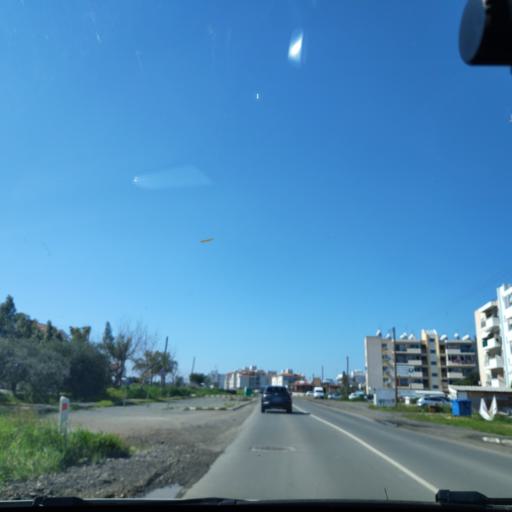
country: CY
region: Lefkosia
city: Tseri
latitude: 35.1129
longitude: 33.3254
